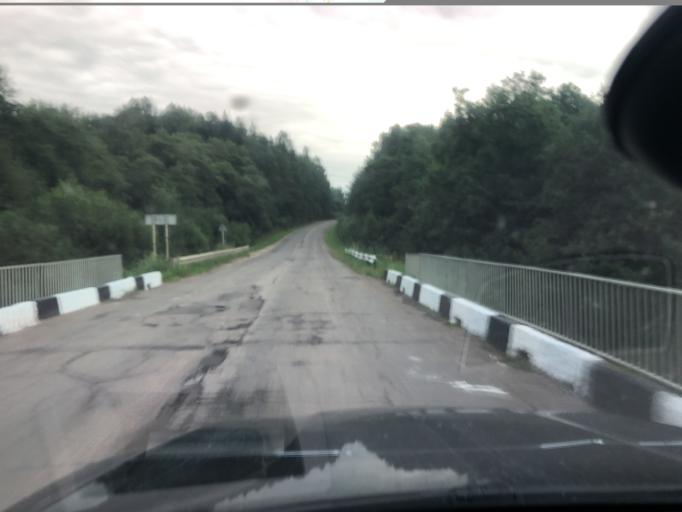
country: RU
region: Jaroslavl
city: Petrovsk
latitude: 56.9987
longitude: 39.0967
